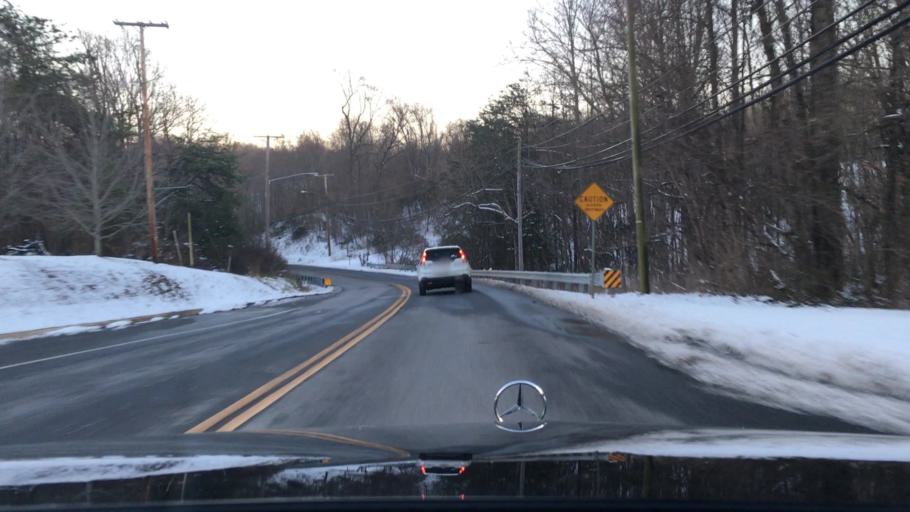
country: US
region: Virginia
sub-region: City of Lynchburg
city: West Lynchburg
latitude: 37.3612
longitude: -79.2012
